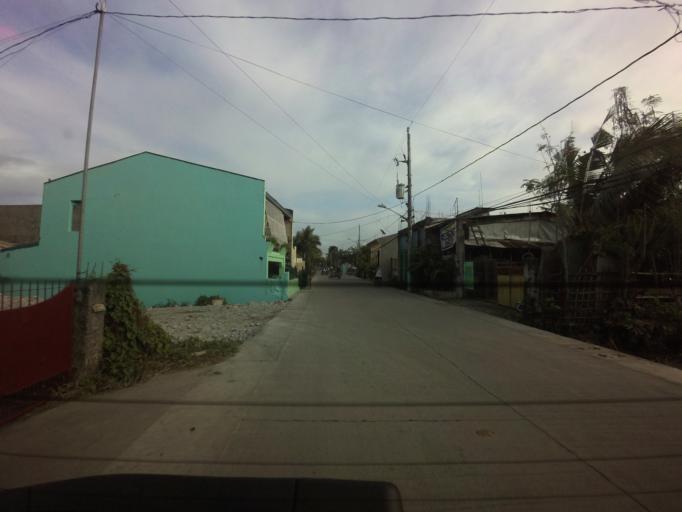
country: PH
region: Central Luzon
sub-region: Province of Bulacan
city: Obando
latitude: 14.7210
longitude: 120.9336
